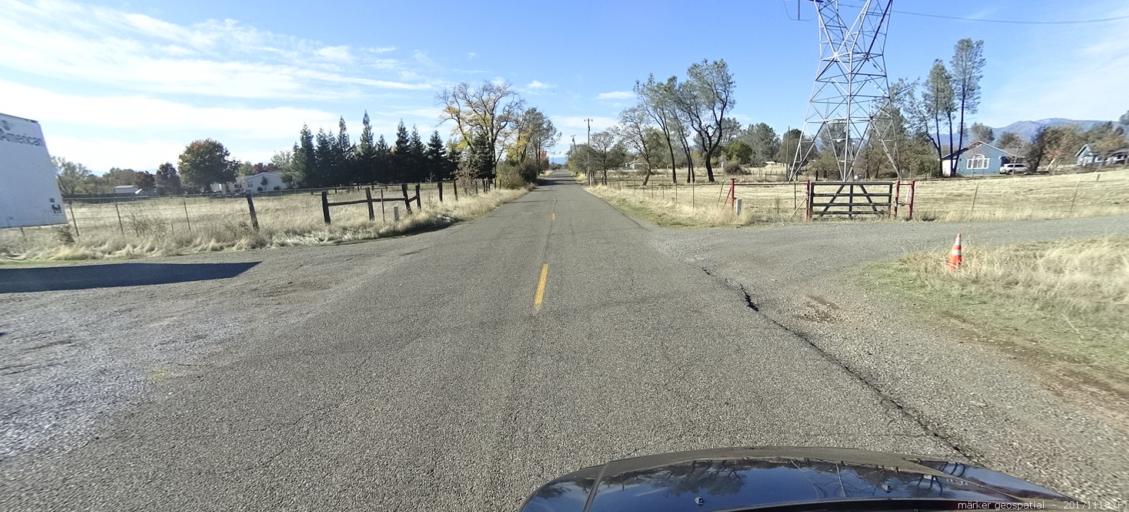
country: US
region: California
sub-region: Shasta County
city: Anderson
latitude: 40.4393
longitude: -122.4154
